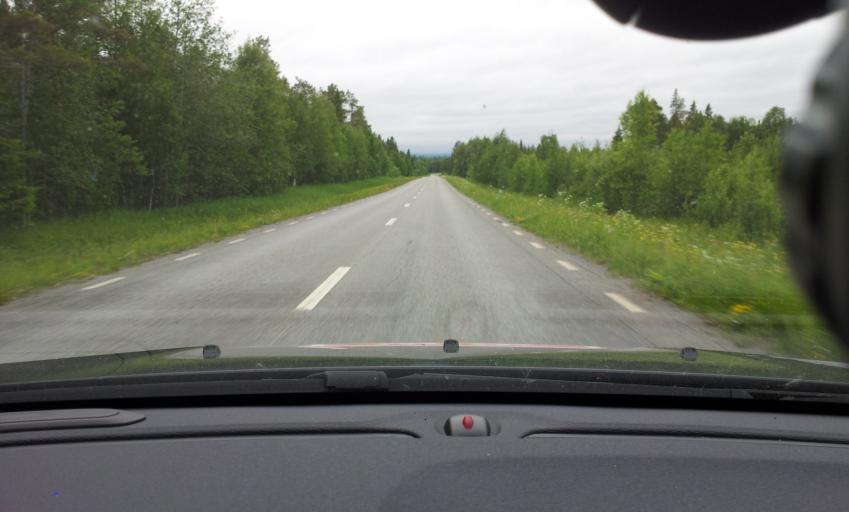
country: SE
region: Jaemtland
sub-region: Krokoms Kommun
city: Krokom
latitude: 63.1318
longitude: 14.2466
